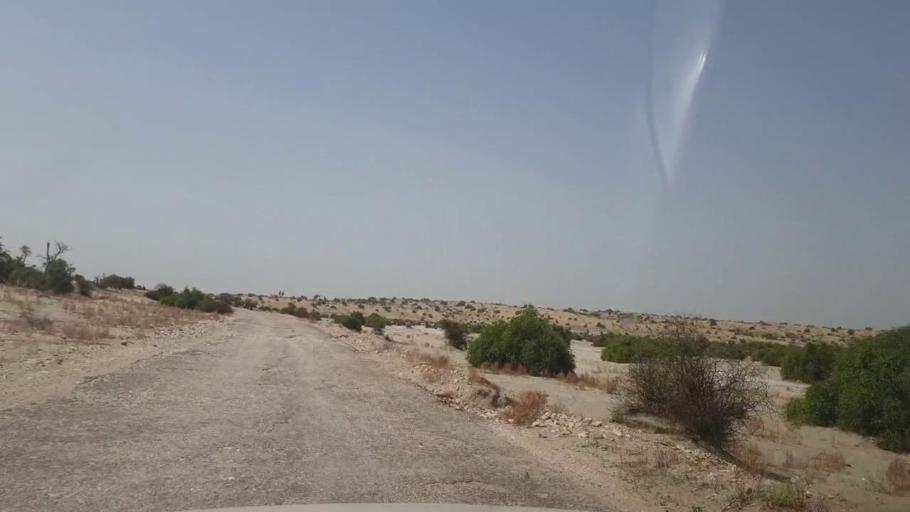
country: PK
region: Sindh
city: Khanpur
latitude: 27.3539
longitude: 69.3177
